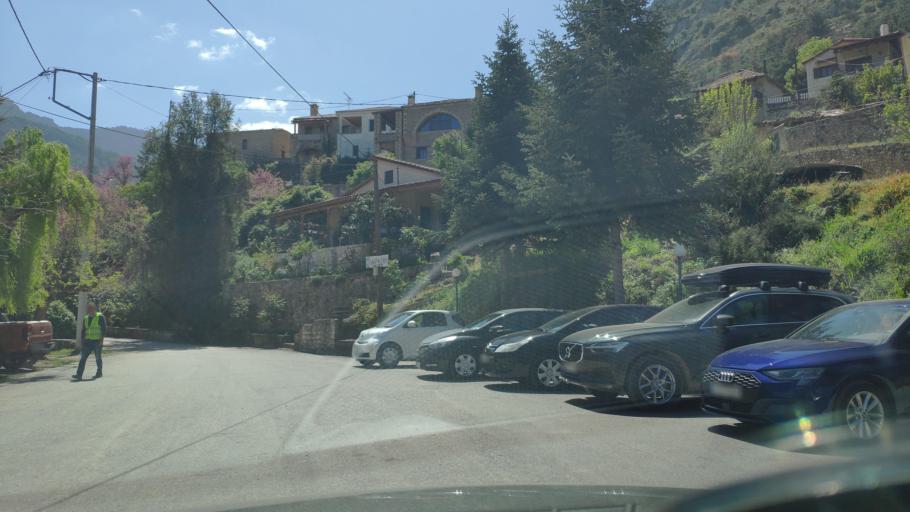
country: GR
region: West Greece
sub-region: Nomos Achaias
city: Aiyira
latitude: 38.0661
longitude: 22.3390
